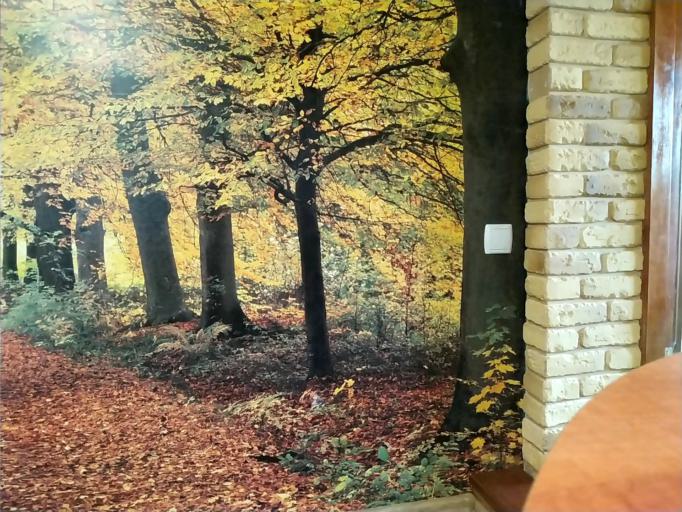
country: RU
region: Leningrad
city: Tolmachevo
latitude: 58.9415
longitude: 29.6706
